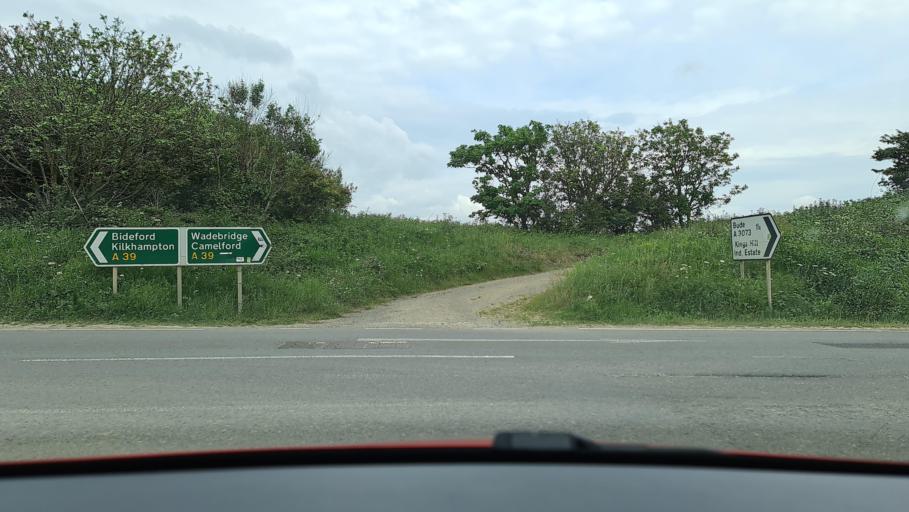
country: GB
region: England
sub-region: Cornwall
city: Bude
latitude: 50.8159
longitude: -4.5286
